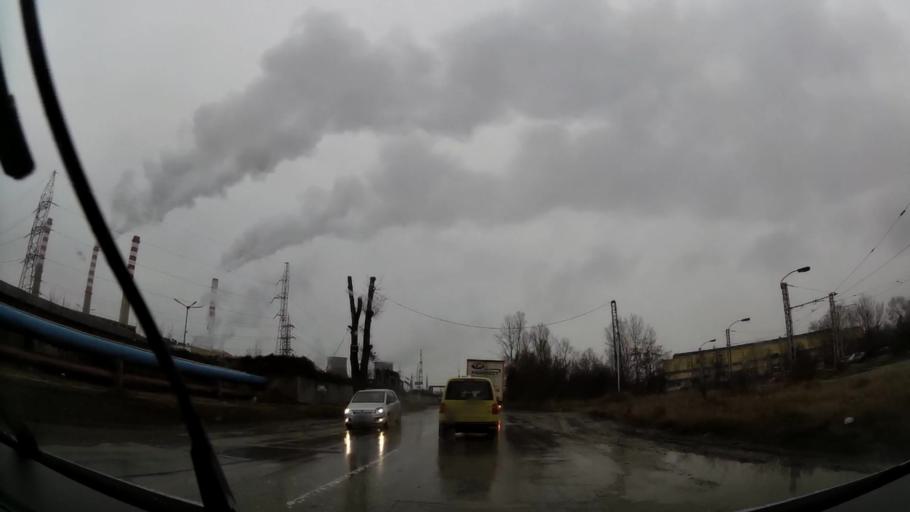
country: BG
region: Sofia-Capital
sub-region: Stolichna Obshtina
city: Sofia
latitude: 42.6555
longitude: 23.4145
